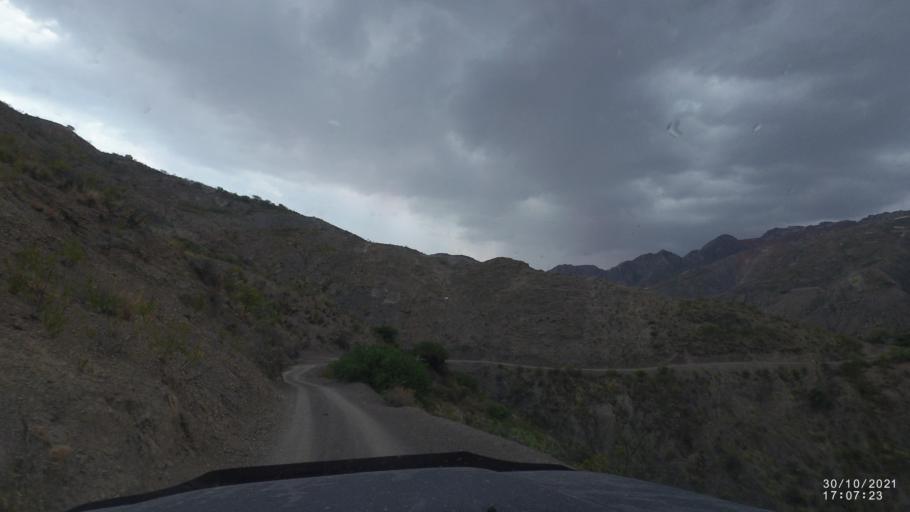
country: BO
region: Cochabamba
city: Colchani
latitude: -17.5638
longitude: -66.6250
